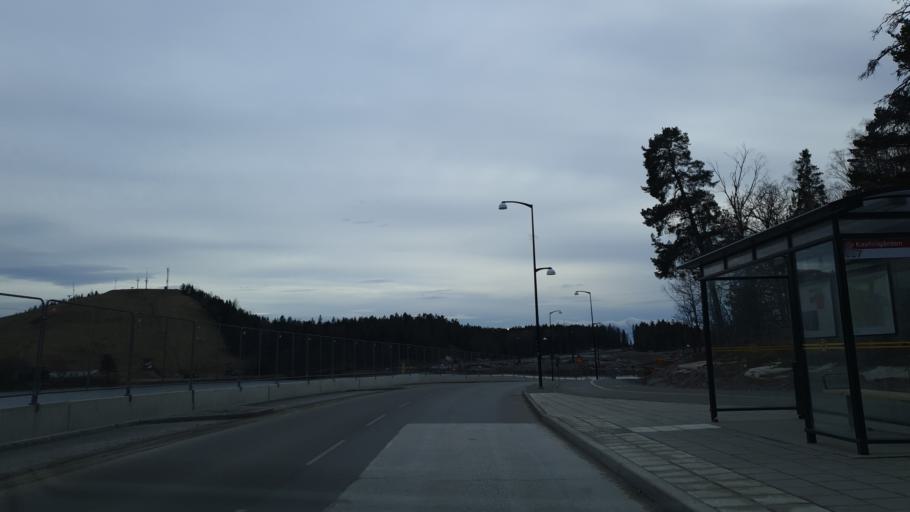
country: SE
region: Stockholm
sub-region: Sollentuna Kommun
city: Sollentuna
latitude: 59.4594
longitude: 17.9717
